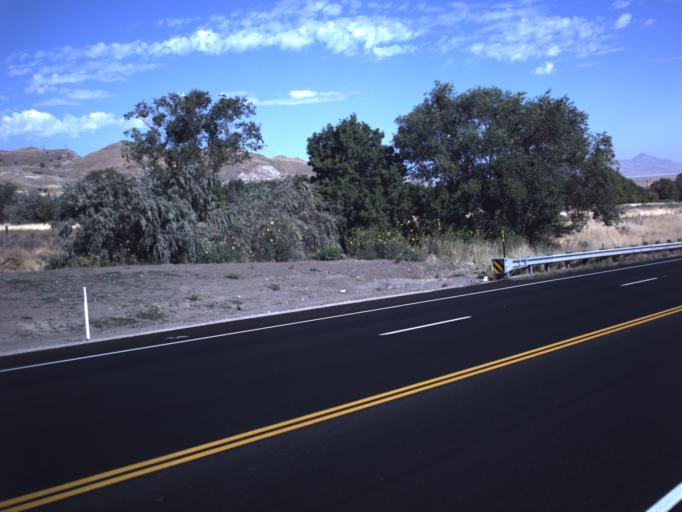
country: US
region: Utah
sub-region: Salt Lake County
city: Magna
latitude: 40.6741
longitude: -112.0919
